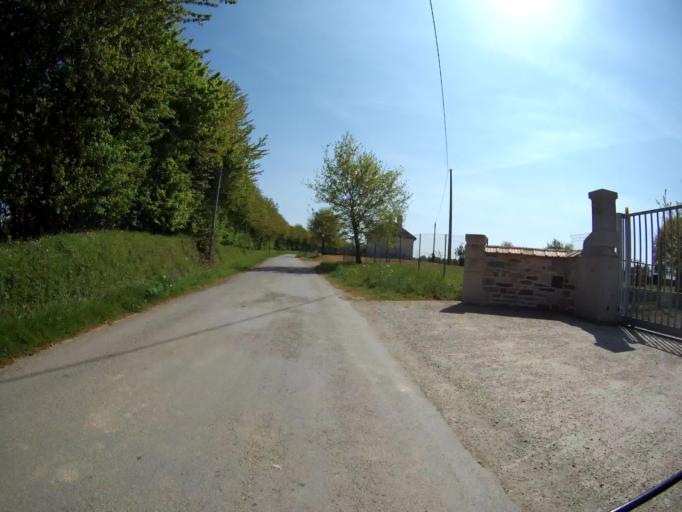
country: FR
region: Brittany
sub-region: Departement d'Ille-et-Vilaine
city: Vern-sur-Seiche
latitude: 48.0313
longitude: -1.6239
